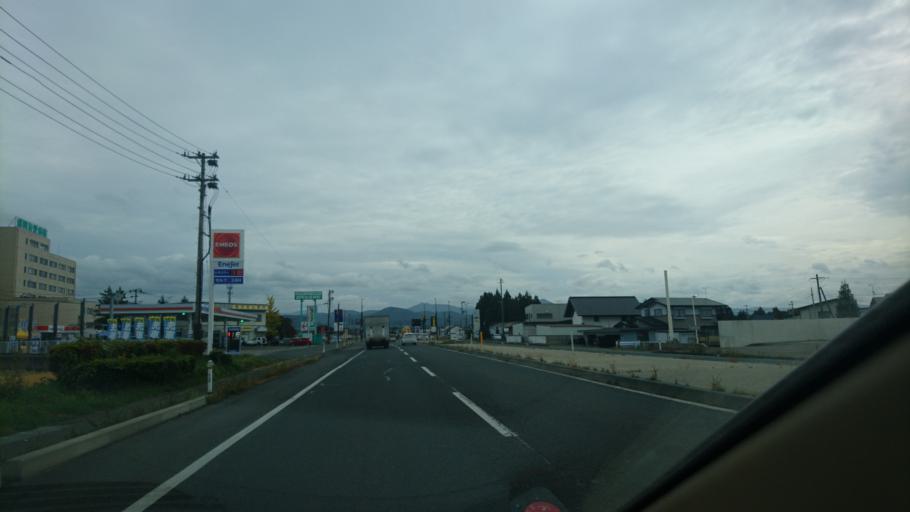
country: JP
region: Iwate
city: Morioka-shi
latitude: 39.6575
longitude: 141.1362
